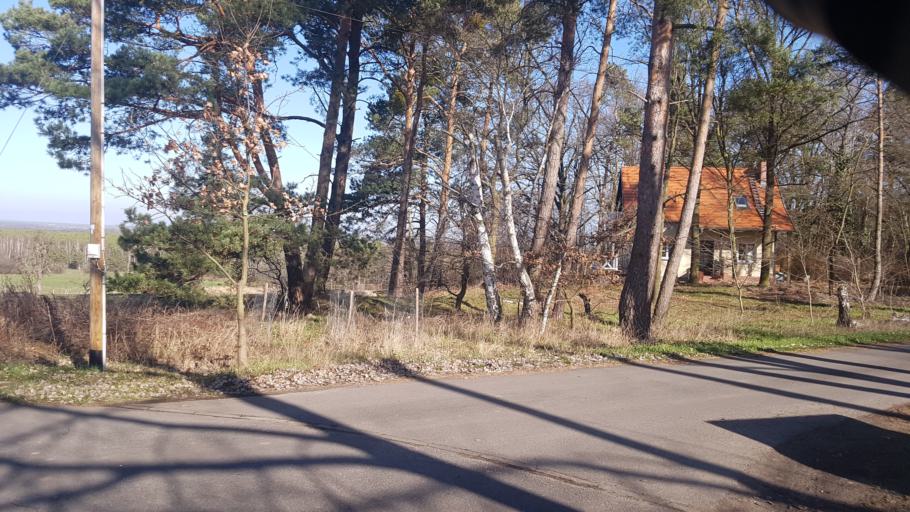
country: DE
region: Brandenburg
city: Crinitz
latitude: 51.7625
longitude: 13.7530
